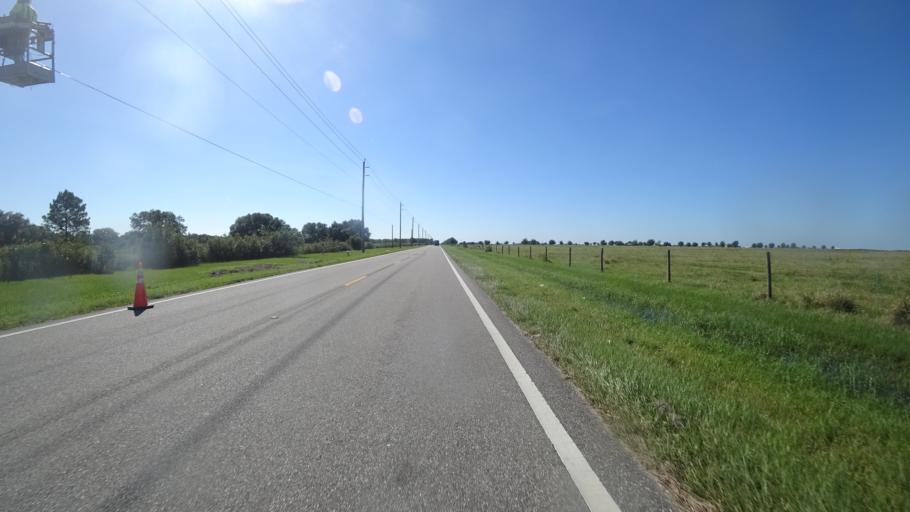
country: US
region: Florida
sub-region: Sarasota County
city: Lake Sarasota
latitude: 27.3779
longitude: -82.2683
